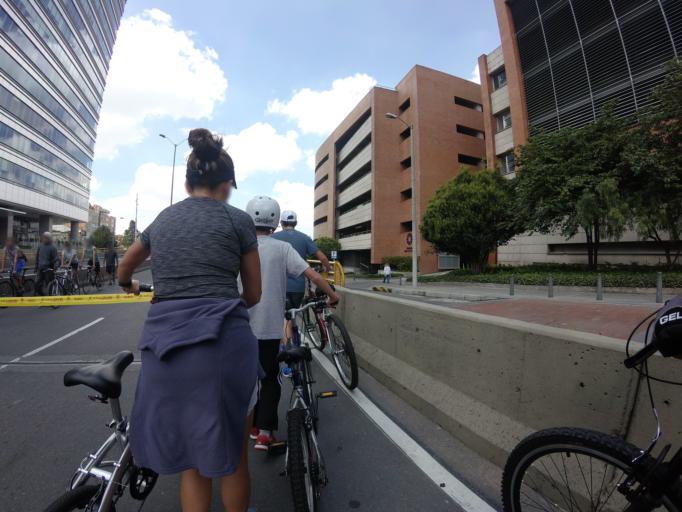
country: CO
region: Bogota D.C.
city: Barrio San Luis
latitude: 4.6939
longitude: -74.0336
